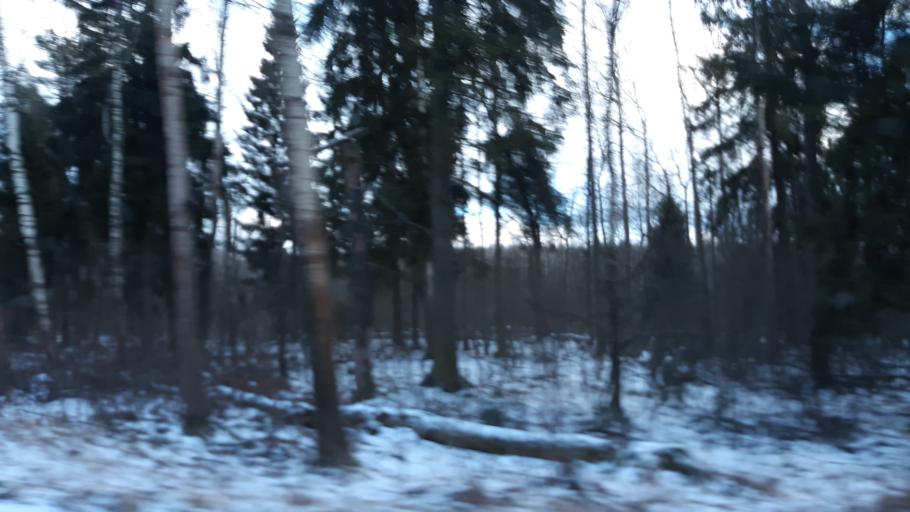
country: RU
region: Moskovskaya
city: Noginsk
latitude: 55.9323
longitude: 38.5439
